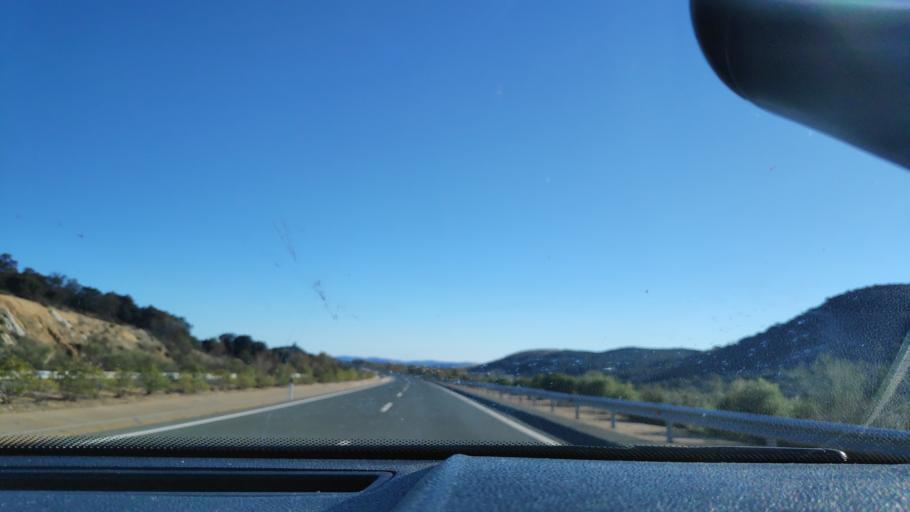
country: ES
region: Extremadura
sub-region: Provincia de Badajoz
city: Monesterio
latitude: 38.0517
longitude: -6.2372
